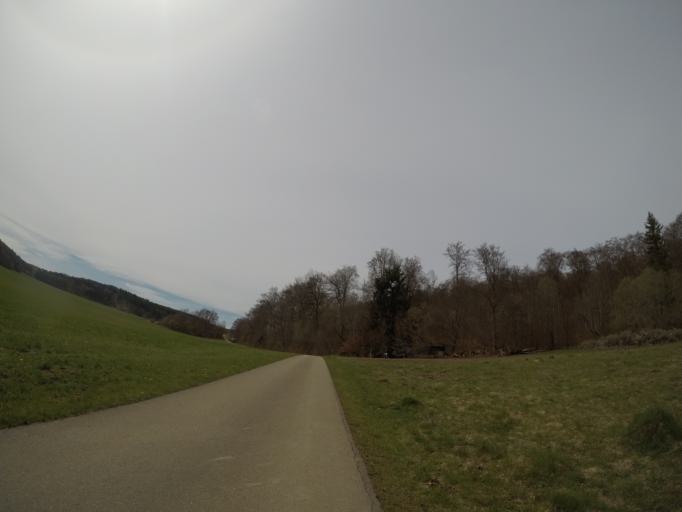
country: DE
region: Baden-Wuerttemberg
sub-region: Regierungsbezirk Stuttgart
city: Neidlingen
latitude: 48.5416
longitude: 9.5579
